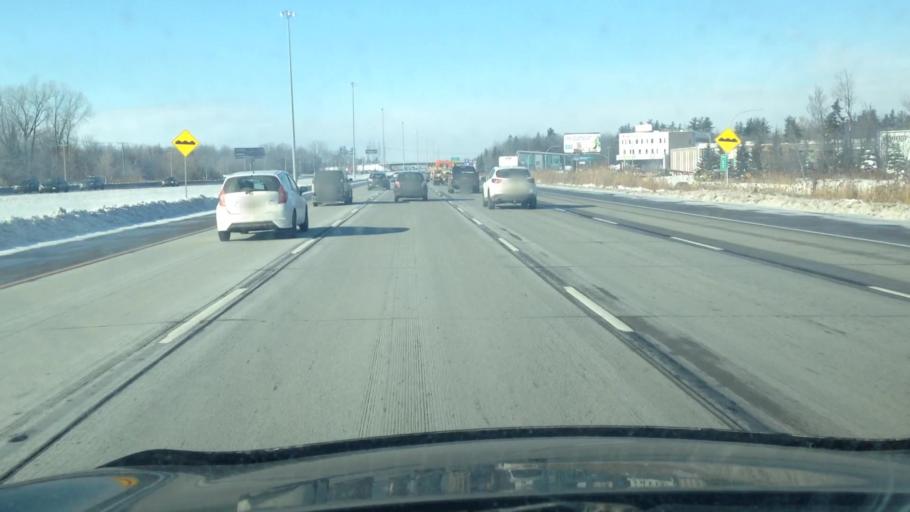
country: CA
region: Quebec
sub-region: Laurentides
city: Blainville
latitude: 45.6705
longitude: -73.9043
